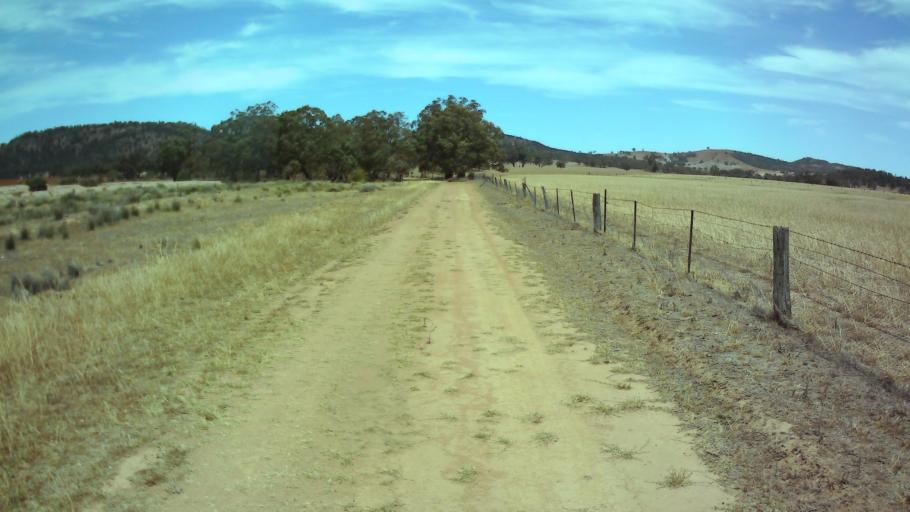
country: AU
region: New South Wales
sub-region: Weddin
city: Grenfell
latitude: -33.7622
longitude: 148.1458
